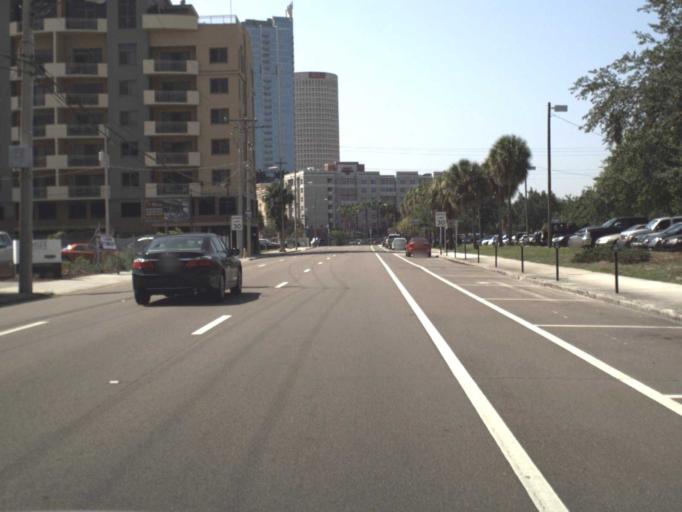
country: US
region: Florida
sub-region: Hillsborough County
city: Tampa
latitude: 27.9543
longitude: -82.4610
